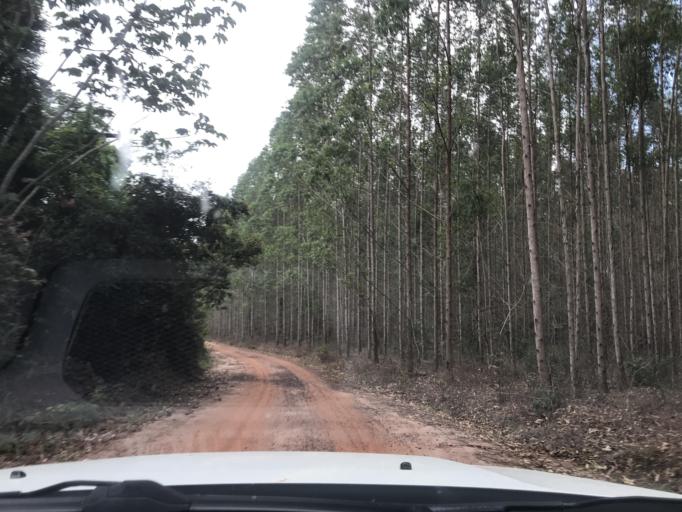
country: BR
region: Bahia
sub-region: Entre Rios
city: Entre Rios
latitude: -12.1006
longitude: -38.1888
